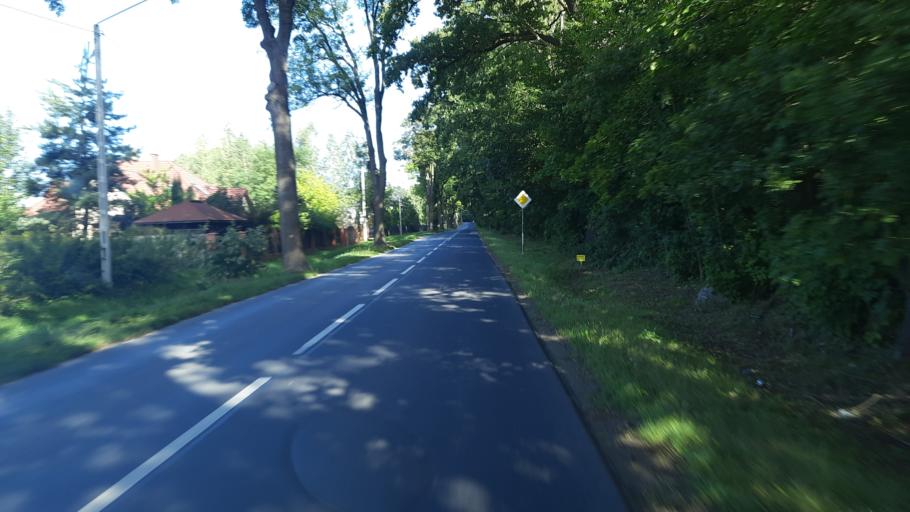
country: PL
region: Lower Silesian Voivodeship
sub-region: Powiat wroclawski
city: Dlugoleka
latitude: 51.1870
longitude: 17.1854
